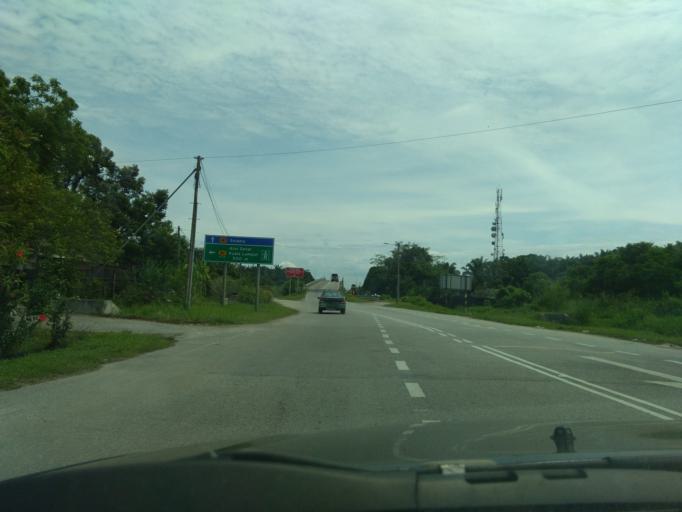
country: MY
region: Perak
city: Bagan Serai
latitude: 5.0608
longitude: 100.5945
